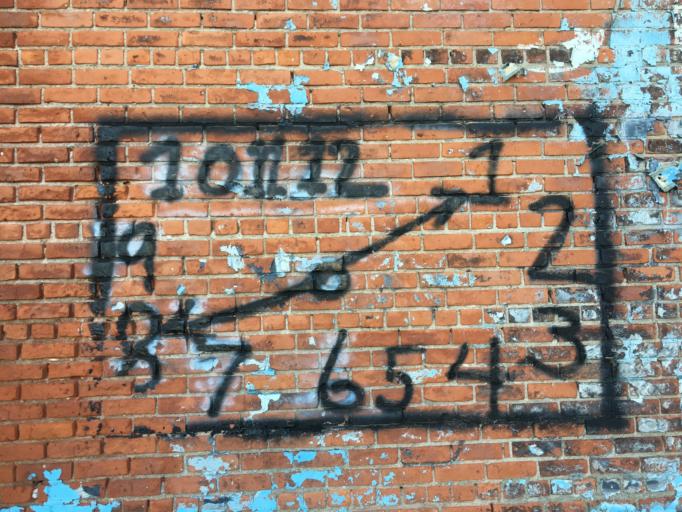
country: US
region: Michigan
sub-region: Wayne County
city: Detroit
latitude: 42.3572
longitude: -83.0180
